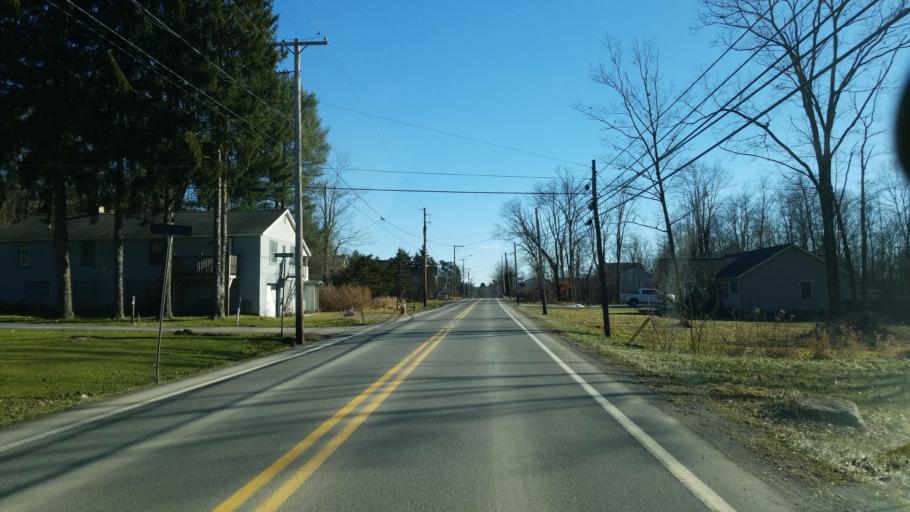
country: US
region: Pennsylvania
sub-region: Jefferson County
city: Falls Creek
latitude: 41.1510
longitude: -78.8140
